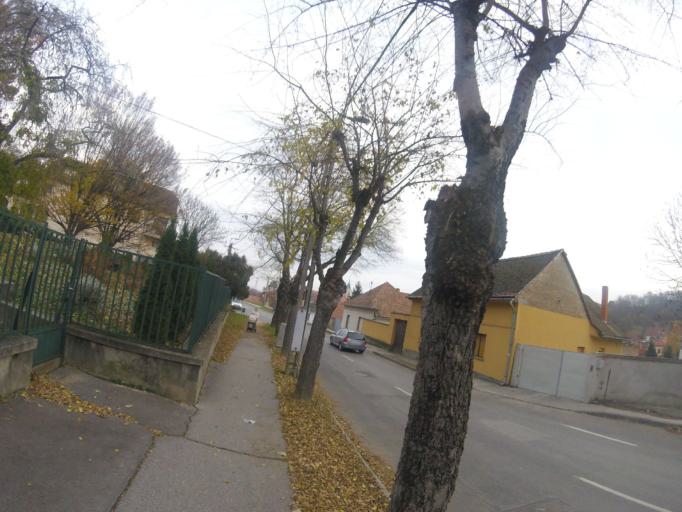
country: HU
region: Tolna
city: Szekszard
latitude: 46.3507
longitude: 18.6937
